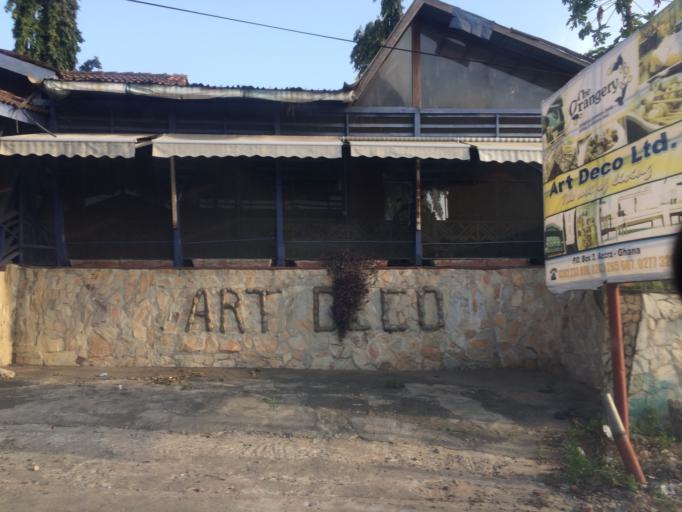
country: GH
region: Greater Accra
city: Accra
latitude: 5.5660
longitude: -0.2111
